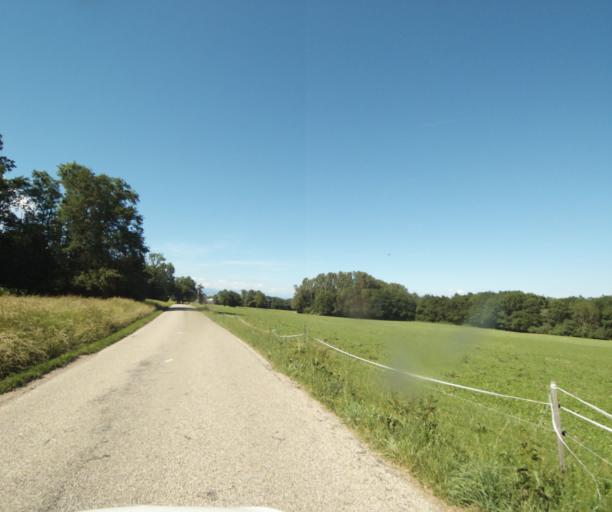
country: FR
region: Rhone-Alpes
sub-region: Departement de la Haute-Savoie
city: Sciez
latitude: 46.3059
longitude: 6.3809
